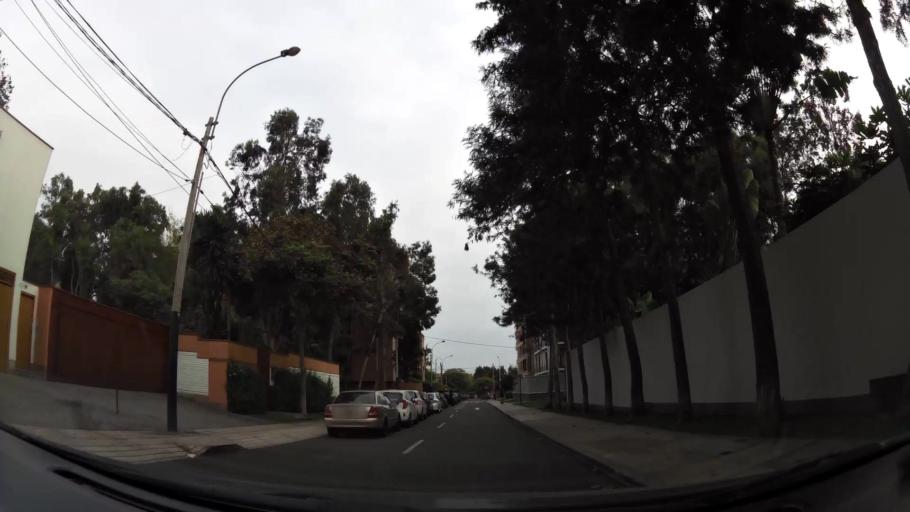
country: PE
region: Lima
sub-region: Lima
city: San Isidro
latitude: -12.1042
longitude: -77.0416
